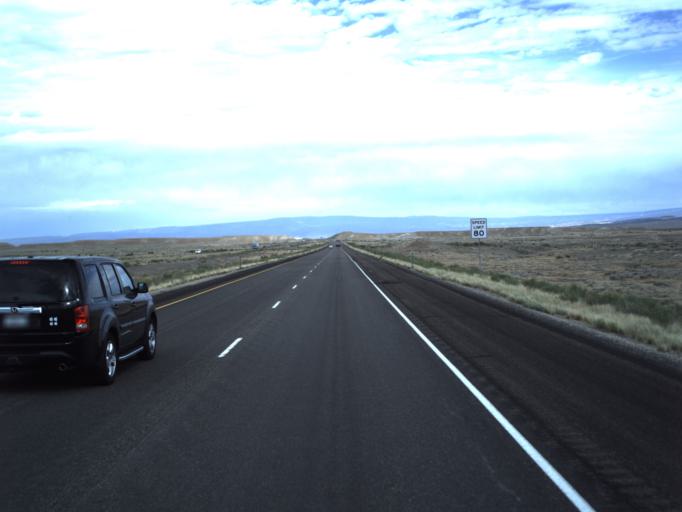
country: US
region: Utah
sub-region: Grand County
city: Moab
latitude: 38.9466
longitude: -109.6591
